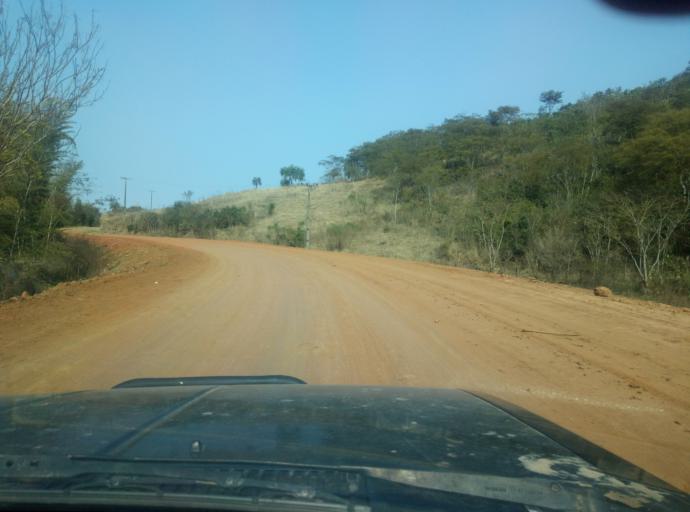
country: PY
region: Caaguazu
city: Coronel Oviedo
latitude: -25.3387
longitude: -56.3157
